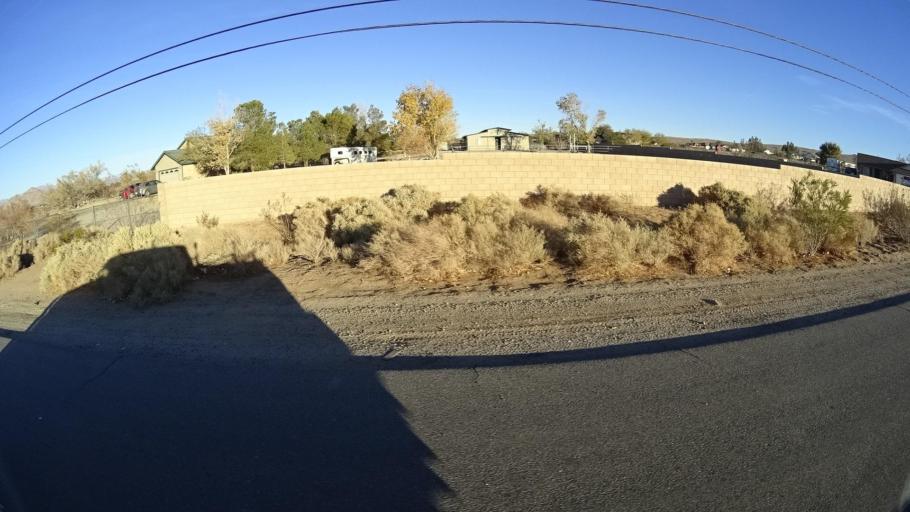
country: US
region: California
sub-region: Kern County
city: Ridgecrest
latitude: 35.6000
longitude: -117.6527
